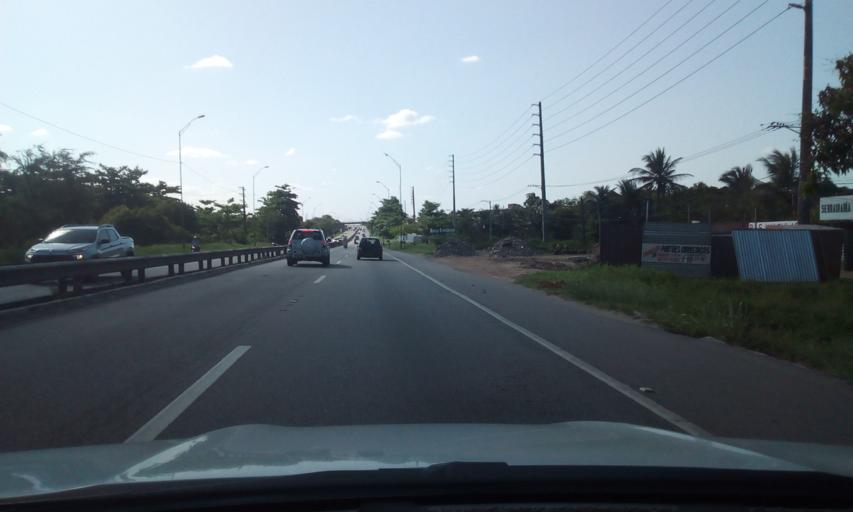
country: BR
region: Paraiba
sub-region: Bayeux
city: Bayeux
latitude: -7.1388
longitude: -34.9239
